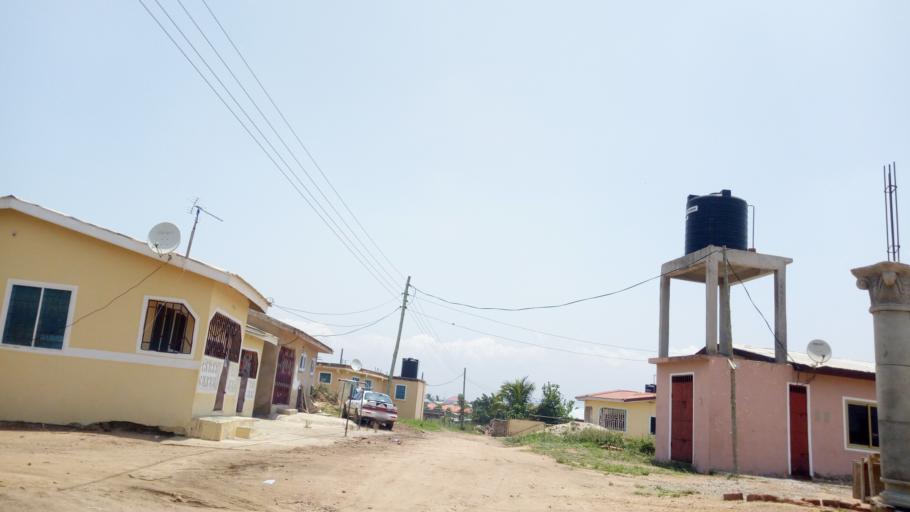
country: GH
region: Central
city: Kasoa
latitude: 5.5039
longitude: -0.4519
